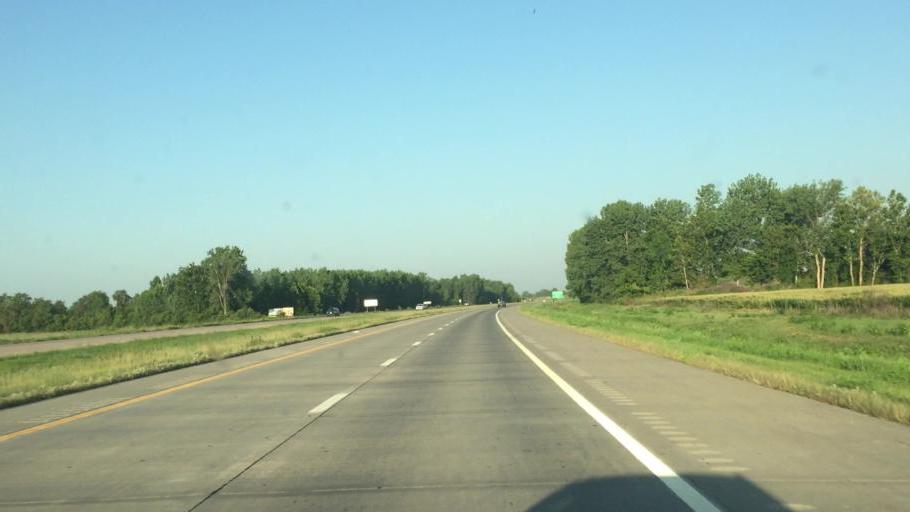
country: US
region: Kansas
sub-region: Doniphan County
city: Elwood
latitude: 39.7450
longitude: -94.8803
